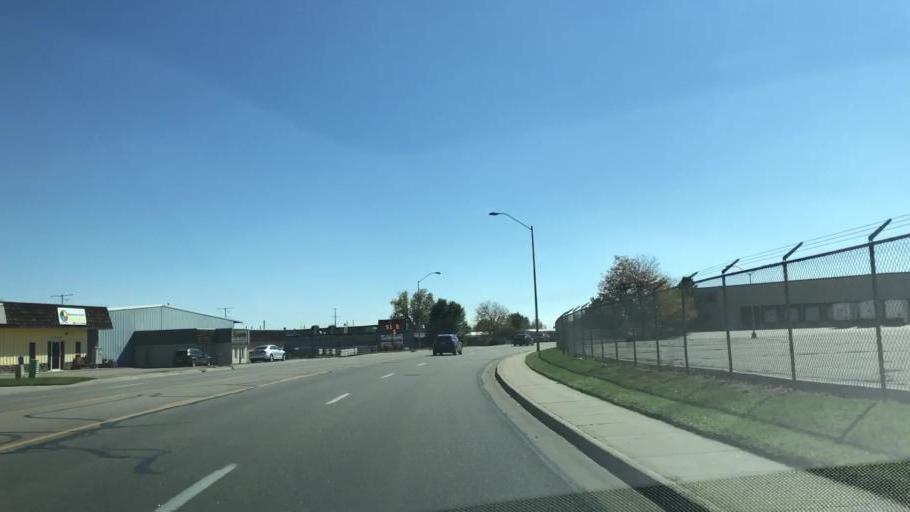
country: US
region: Colorado
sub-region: Larimer County
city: Fort Collins
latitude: 40.5714
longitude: -105.0456
